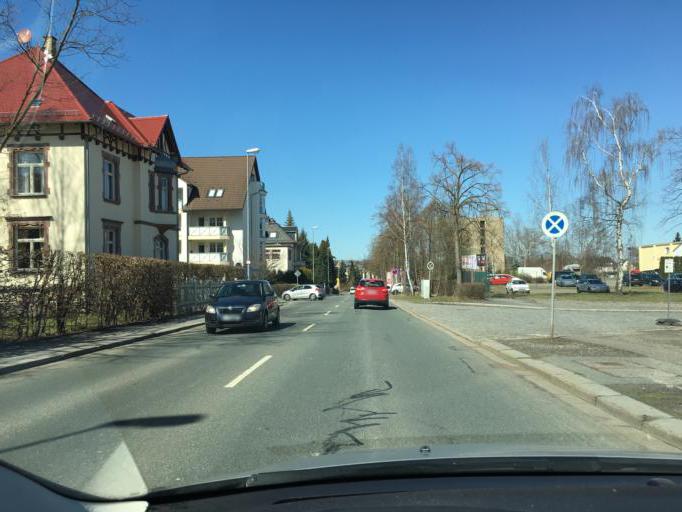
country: DE
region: Saxony
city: Neukirchen
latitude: 50.8099
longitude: 12.8421
